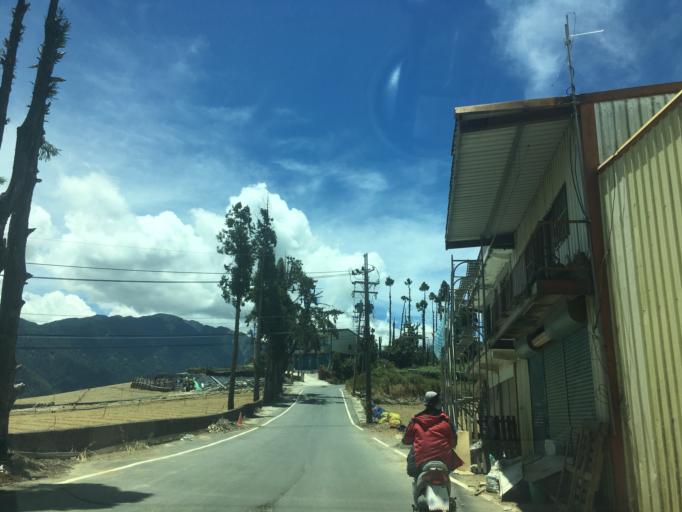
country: TW
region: Taiwan
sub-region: Nantou
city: Puli
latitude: 24.2415
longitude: 121.2462
